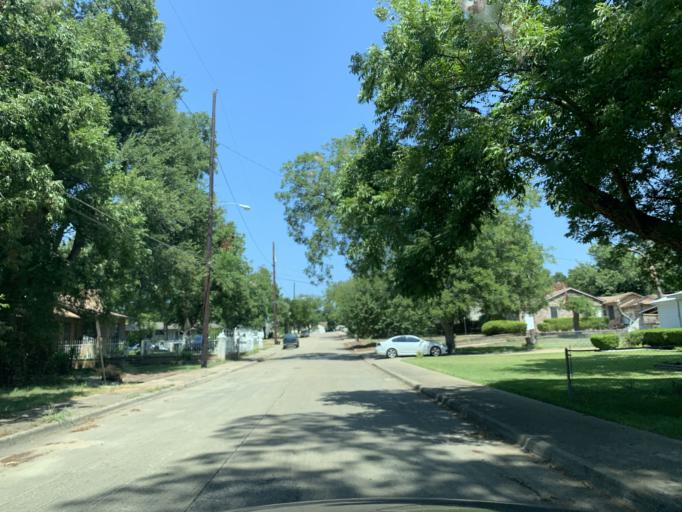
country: US
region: Texas
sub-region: Dallas County
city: Hutchins
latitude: 32.6841
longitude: -96.7916
